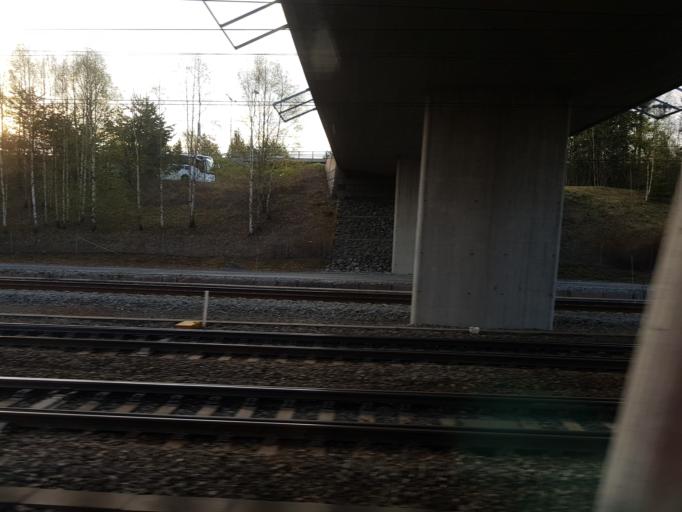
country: NO
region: Akershus
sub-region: Nannestad
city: Teigebyen
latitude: 60.1892
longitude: 11.0944
